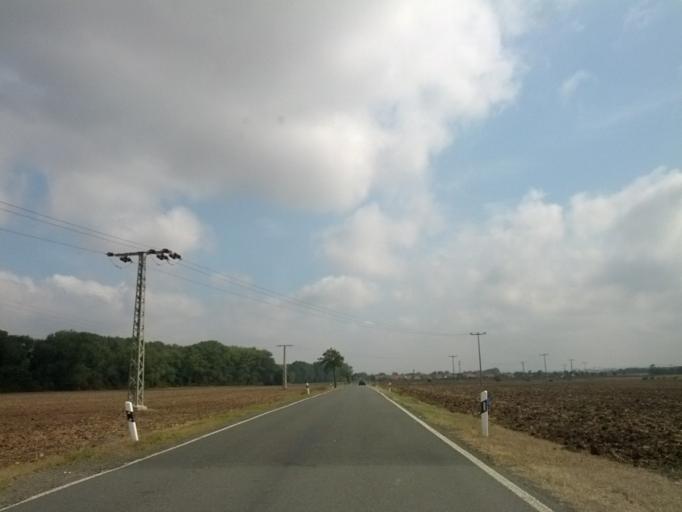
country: DE
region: Thuringia
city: Wandersleben
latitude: 50.9012
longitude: 10.8251
